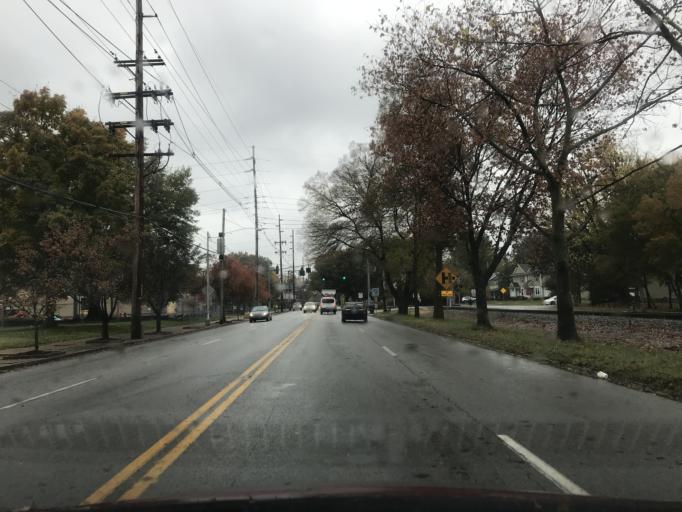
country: US
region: Kentucky
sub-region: Jefferson County
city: Indian Hills
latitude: 38.2546
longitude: -85.6833
